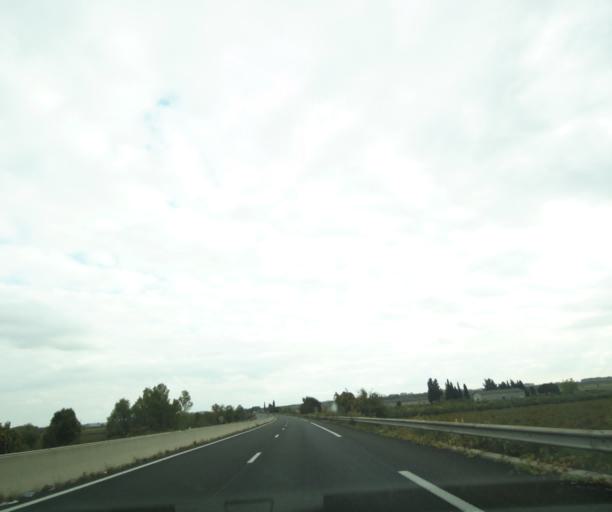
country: FR
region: Languedoc-Roussillon
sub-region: Departement du Gard
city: Gallargues-le-Montueux
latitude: 43.7158
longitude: 4.1837
